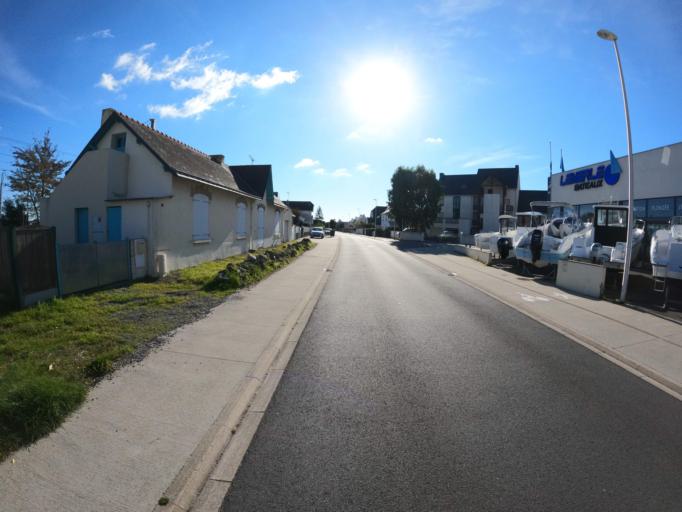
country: FR
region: Pays de la Loire
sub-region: Departement de la Loire-Atlantique
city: Le Croisic
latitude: 47.2879
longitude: -2.5060
